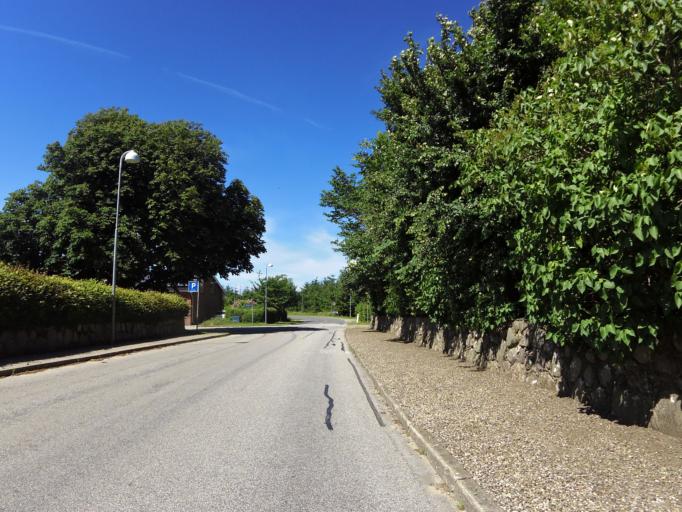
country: DK
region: South Denmark
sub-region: Aabenraa Kommune
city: Rodekro
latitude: 55.0329
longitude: 9.3040
